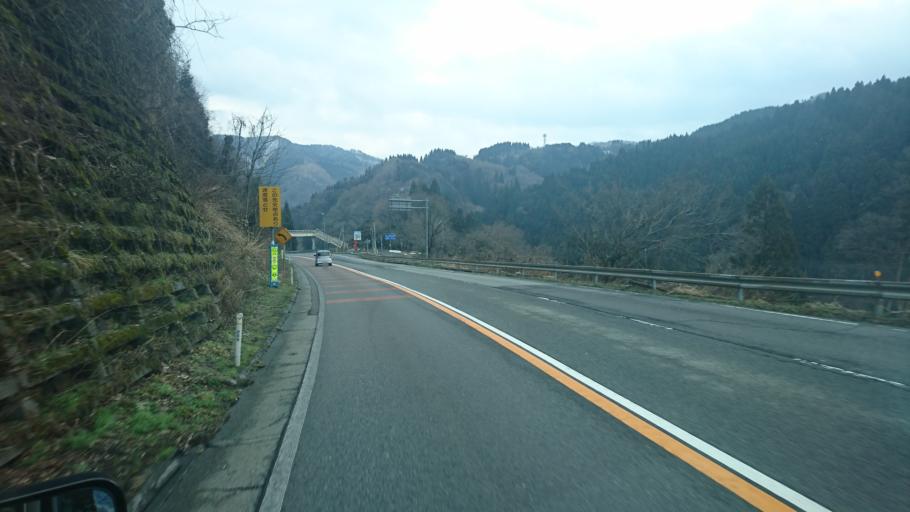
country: JP
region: Hyogo
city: Toyooka
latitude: 35.4929
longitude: 134.5410
